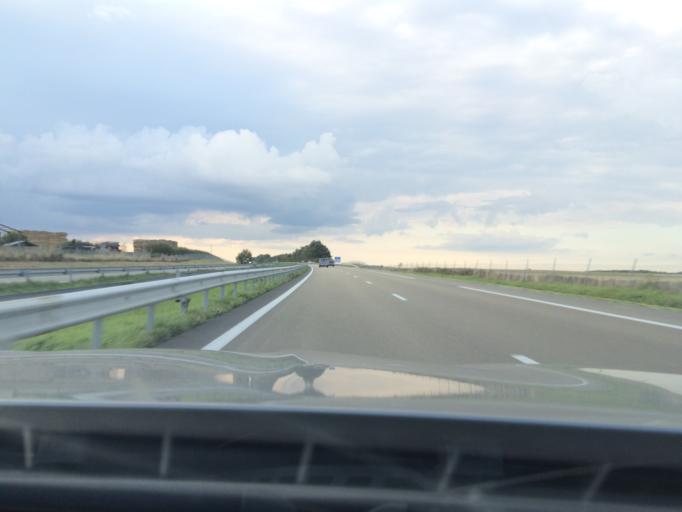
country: FR
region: Ile-de-France
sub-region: Departement de Seine-et-Marne
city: Egreville
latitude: 48.1524
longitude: 2.8984
